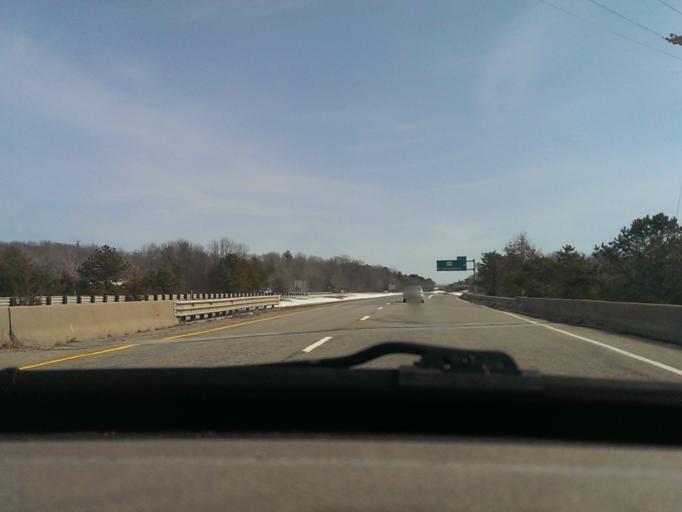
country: US
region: Massachusetts
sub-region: Worcester County
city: Millville
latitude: 42.0236
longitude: -71.6037
